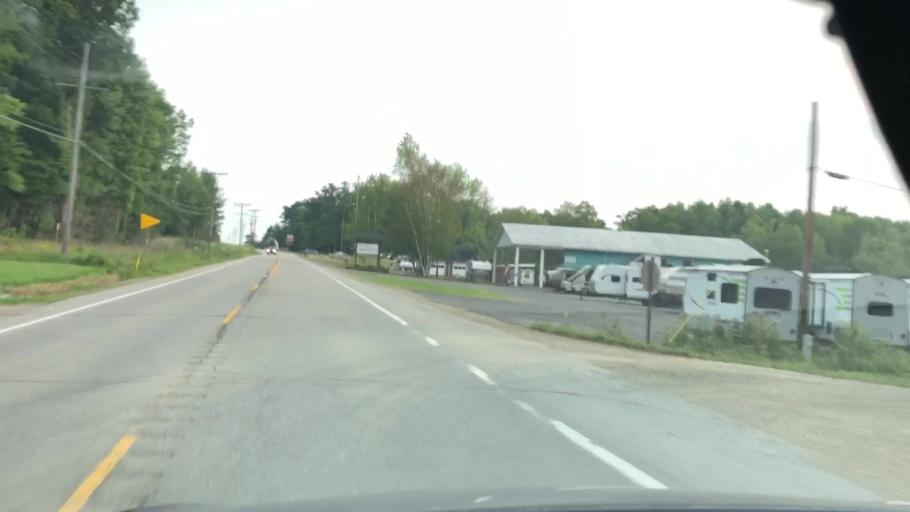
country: US
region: Pennsylvania
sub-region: Crawford County
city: Titusville
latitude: 41.5913
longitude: -79.6838
